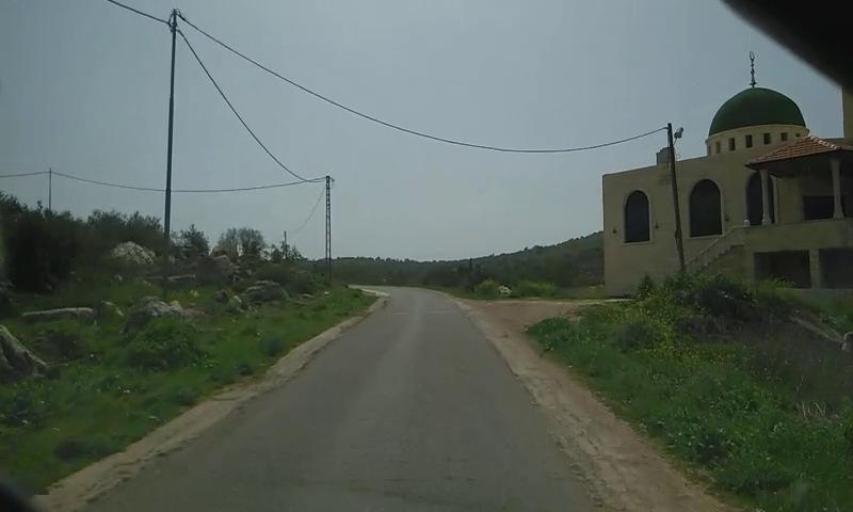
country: PS
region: West Bank
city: At Taybah
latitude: 32.5033
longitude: 35.1978
